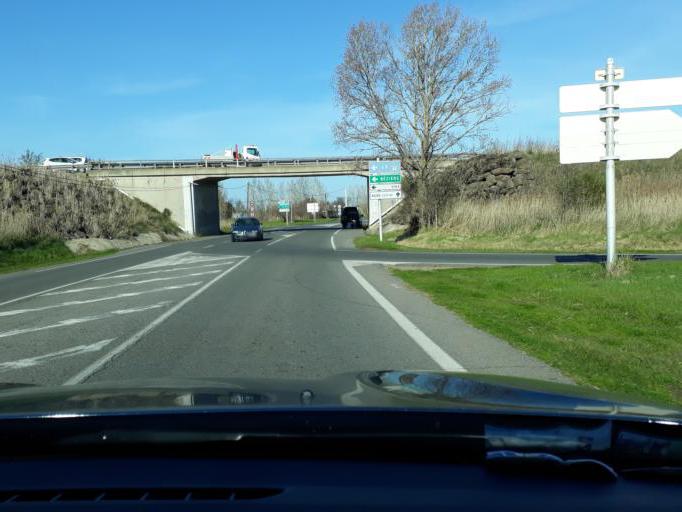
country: FR
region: Languedoc-Roussillon
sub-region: Departement de l'Herault
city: Agde
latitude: 43.3035
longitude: 3.4555
